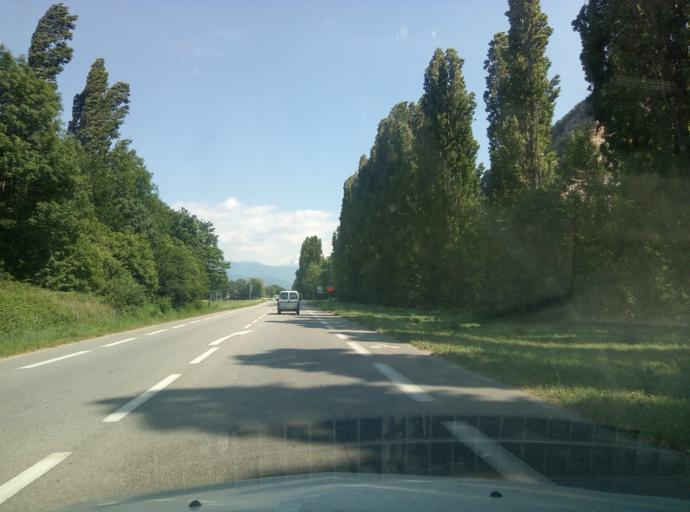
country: FR
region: Rhone-Alpes
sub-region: Departement de l'Isere
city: Noyarey
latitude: 45.2337
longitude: 5.6425
